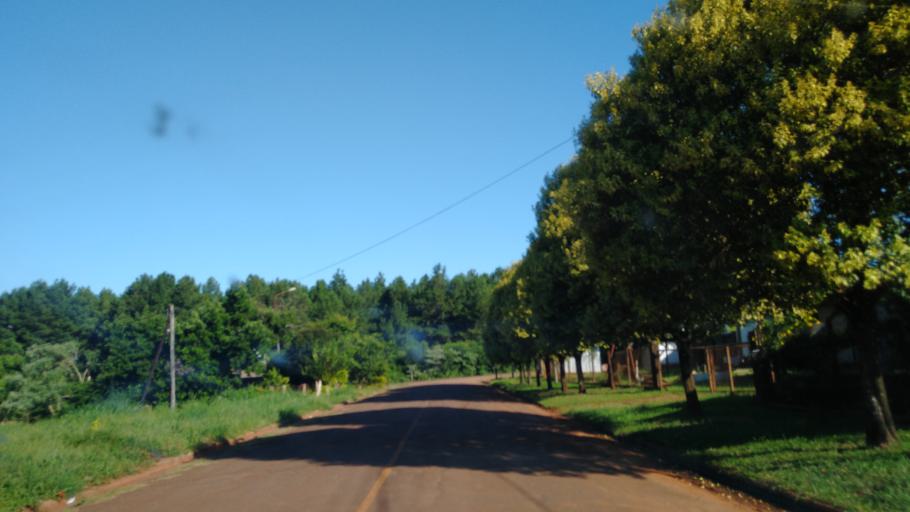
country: AR
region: Misiones
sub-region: Departamento de San Ignacio
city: San Ignacio
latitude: -27.2644
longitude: -55.5368
